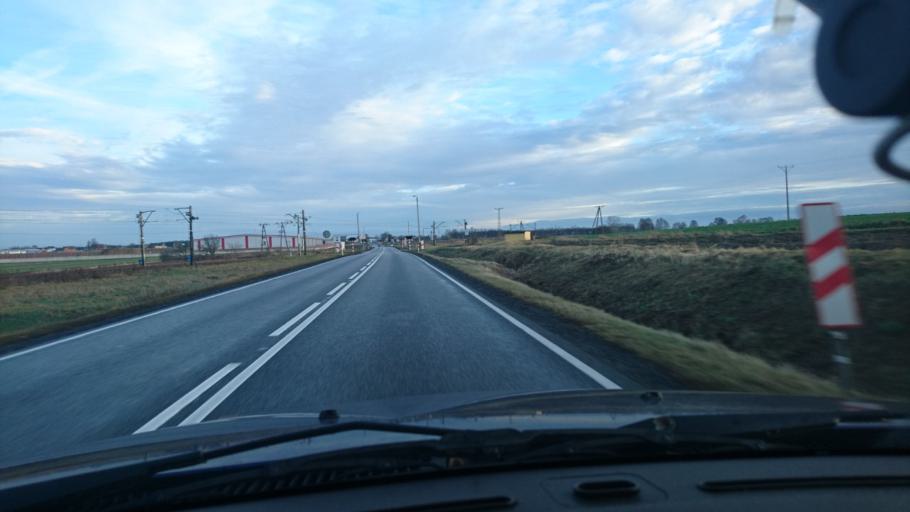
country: PL
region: Greater Poland Voivodeship
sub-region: Powiat kepinski
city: Slupia pod Kepnem
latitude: 51.2332
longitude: 18.0630
